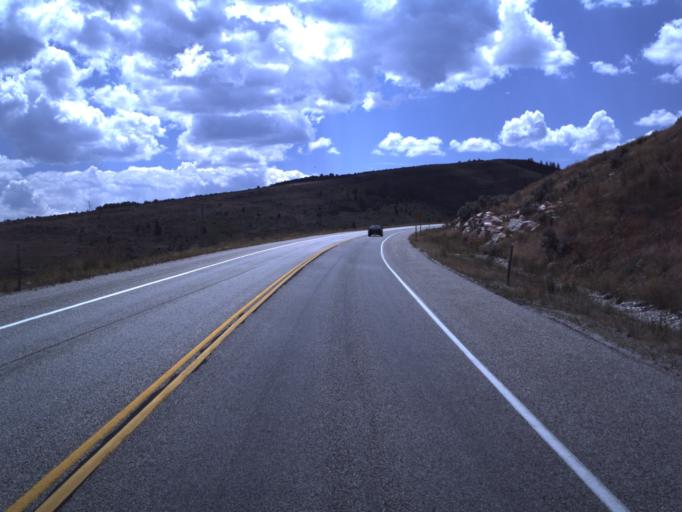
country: US
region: Idaho
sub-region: Bear Lake County
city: Paris
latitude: 41.9385
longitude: -111.4107
